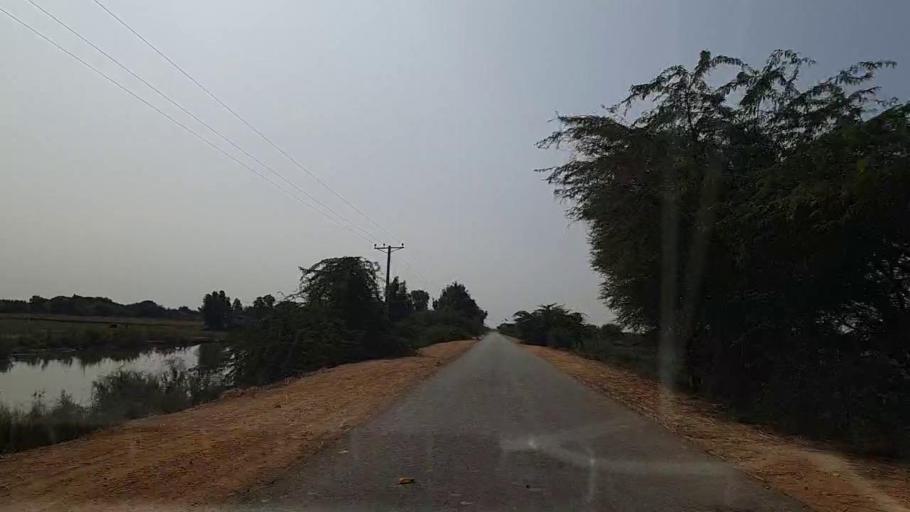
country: PK
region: Sindh
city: Chuhar Jamali
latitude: 24.3603
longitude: 67.9599
